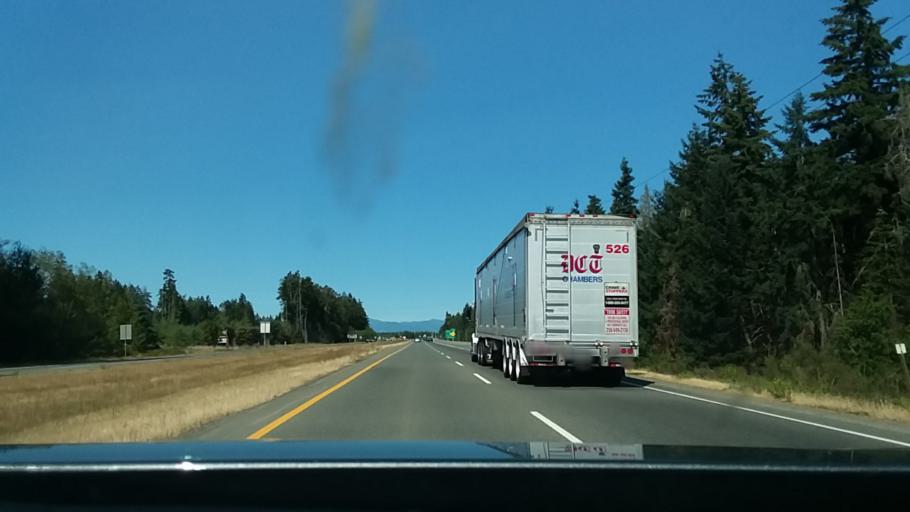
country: CA
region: British Columbia
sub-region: Regional District of Nanaimo
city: Parksville
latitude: 49.3033
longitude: -124.3087
